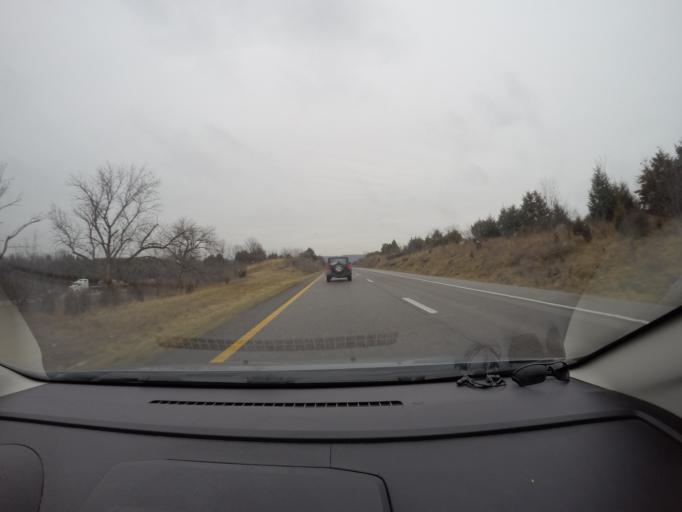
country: US
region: Missouri
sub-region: Montgomery County
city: Montgomery City
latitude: 38.8955
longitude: -91.6095
